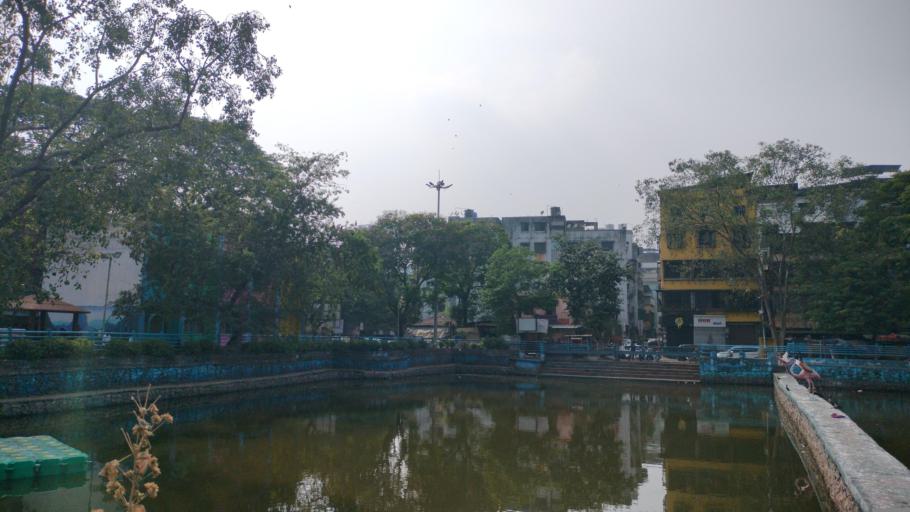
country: IN
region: Maharashtra
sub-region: Thane
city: Navi Mumbai
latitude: 19.0695
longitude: 73.0129
